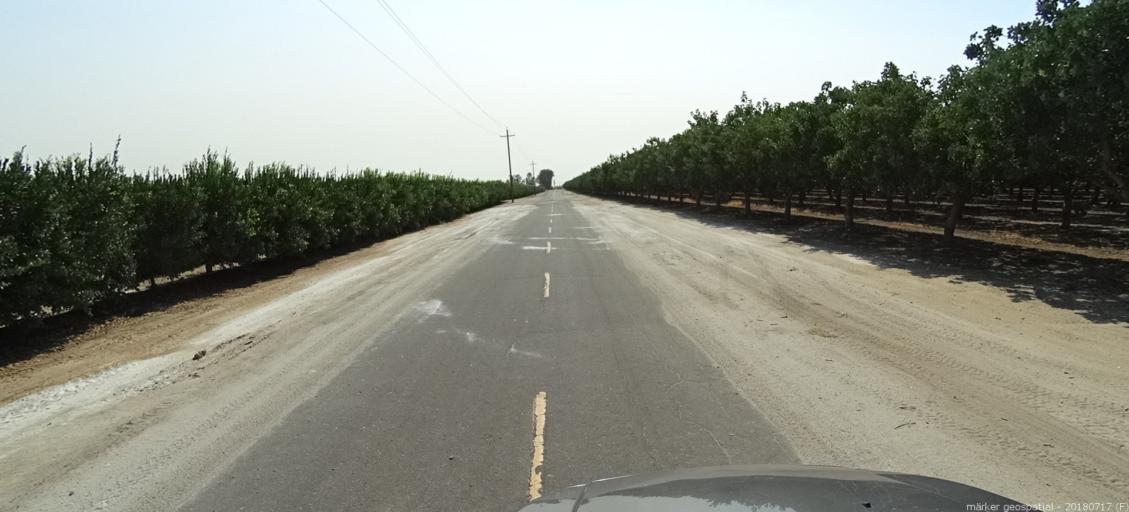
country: US
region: California
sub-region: Madera County
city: Fairmead
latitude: 37.0546
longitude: -120.1527
